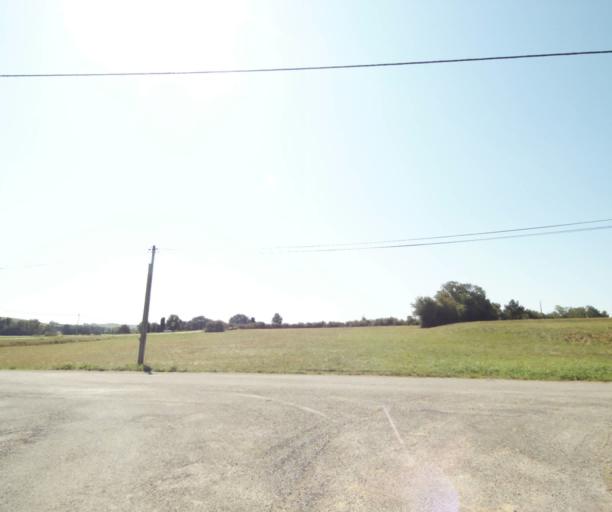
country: FR
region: Midi-Pyrenees
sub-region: Departement de l'Ariege
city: Lezat-sur-Leze
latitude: 43.2983
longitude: 1.3364
